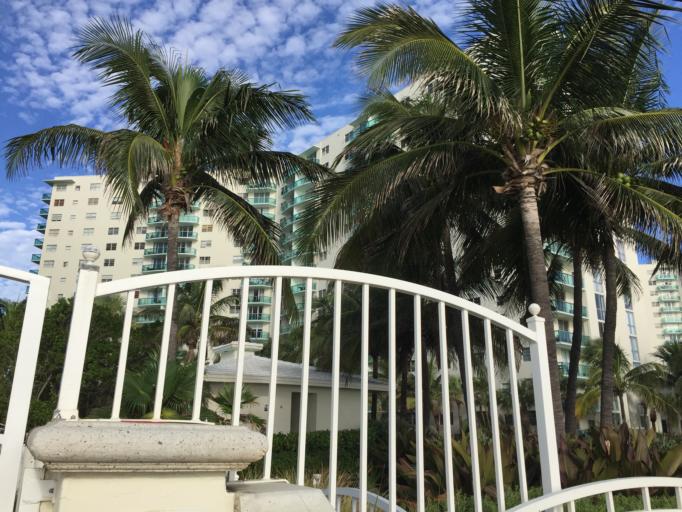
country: US
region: Florida
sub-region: Broward County
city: Hallandale Beach
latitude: 25.9877
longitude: -80.1174
